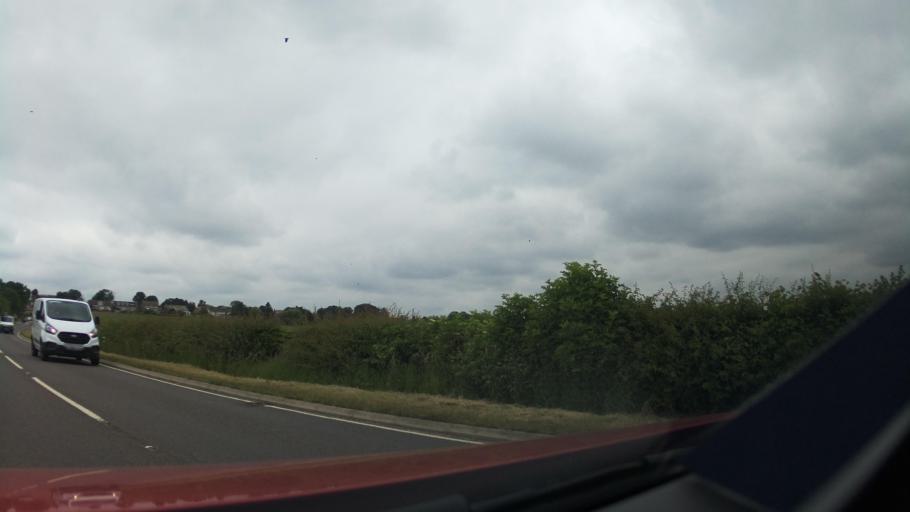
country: GB
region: England
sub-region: Leicestershire
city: Melton Mowbray
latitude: 52.7392
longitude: -0.8598
